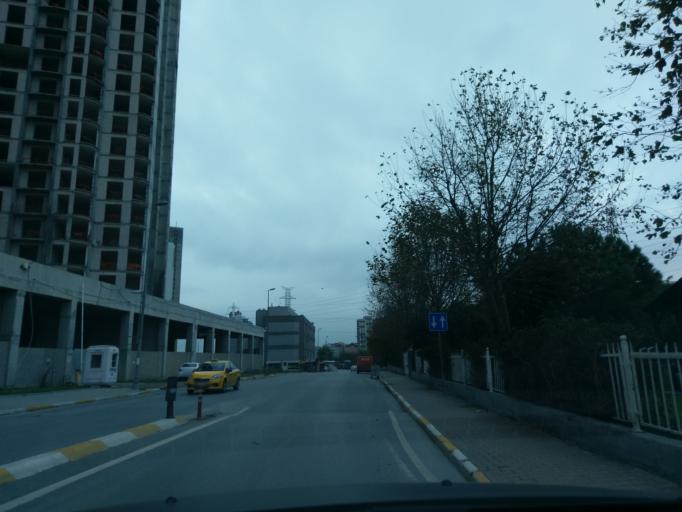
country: TR
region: Istanbul
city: Esenyurt
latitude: 41.0188
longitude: 28.6721
